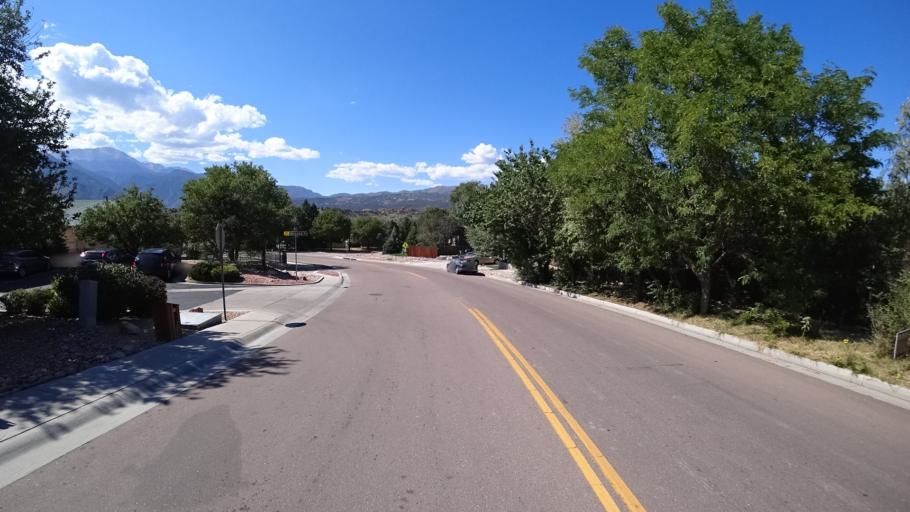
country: US
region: Colorado
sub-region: El Paso County
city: Colorado Springs
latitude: 38.8566
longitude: -104.8628
